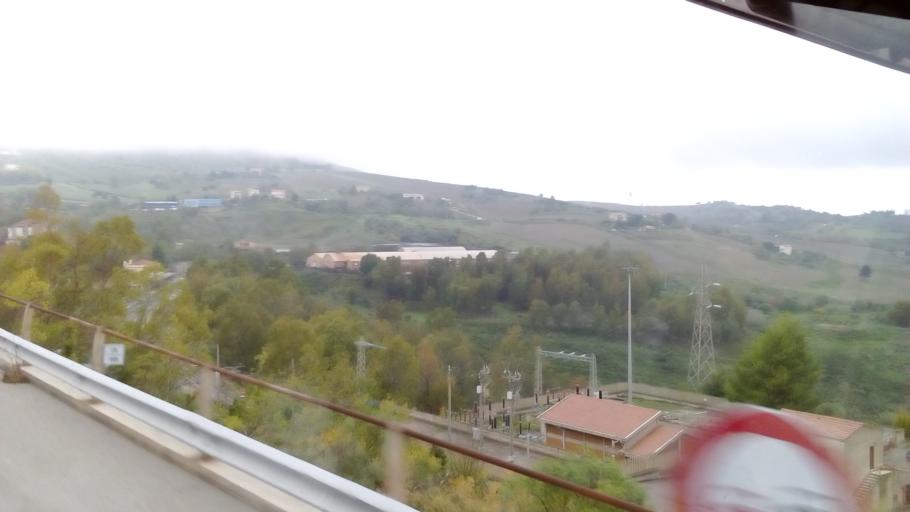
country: IT
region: Sicily
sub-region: Enna
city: Enna
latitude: 37.5788
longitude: 14.2937
